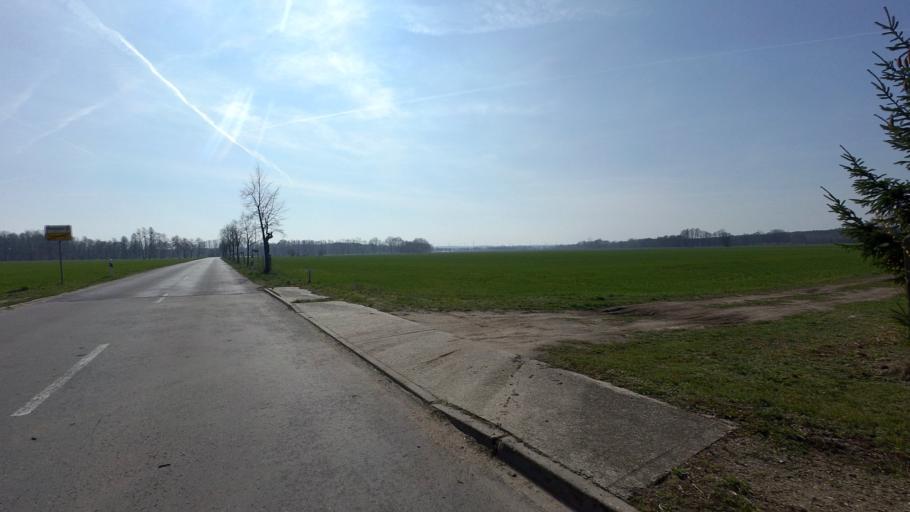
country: DE
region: Brandenburg
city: Drahnsdorf
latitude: 51.9304
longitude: 13.5953
